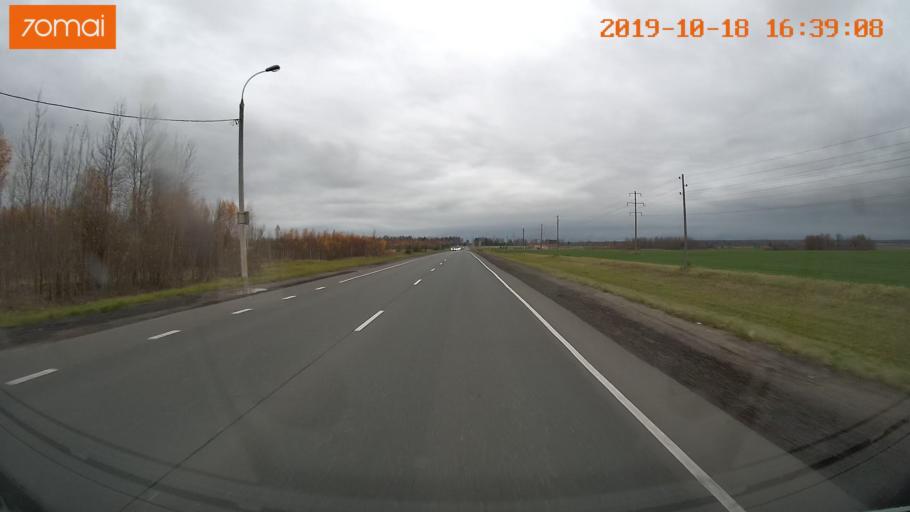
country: RU
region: Vladimir
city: Suzdal'
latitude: 56.4463
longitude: 40.4631
